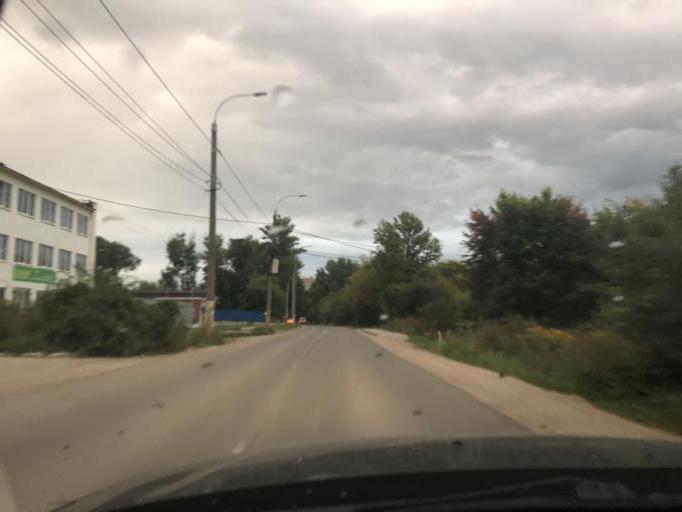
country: RU
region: Tula
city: Gorelki
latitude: 54.2260
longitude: 37.6037
